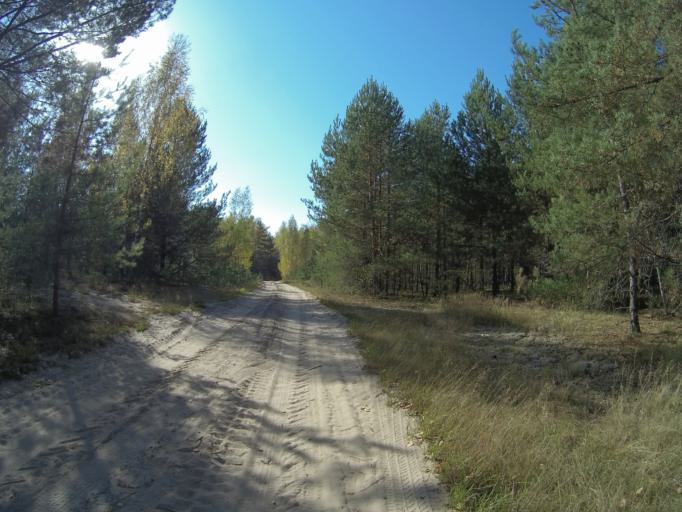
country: RU
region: Vladimir
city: Vorsha
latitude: 55.9698
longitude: 40.1644
